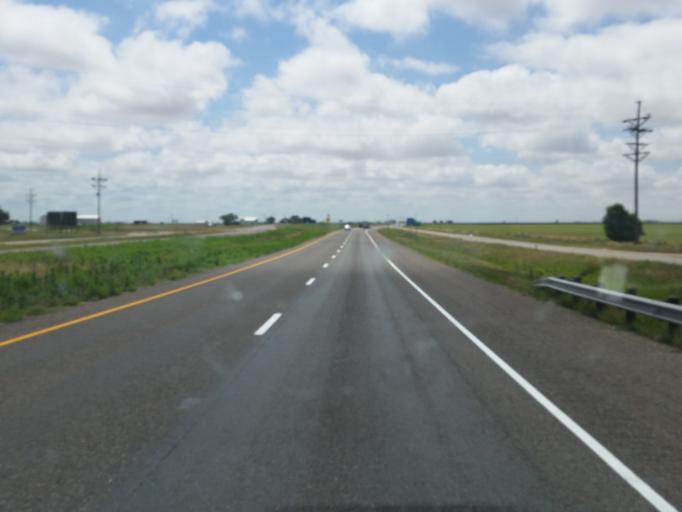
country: US
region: Texas
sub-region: Lubbock County
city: Slaton
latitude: 33.4188
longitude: -101.6410
